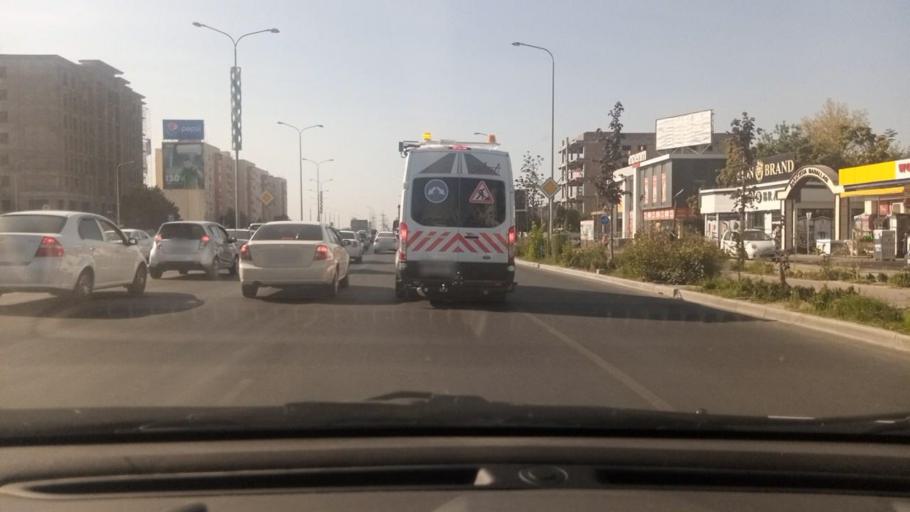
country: UZ
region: Toshkent Shahri
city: Bektemir
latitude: 41.2424
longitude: 69.3280
